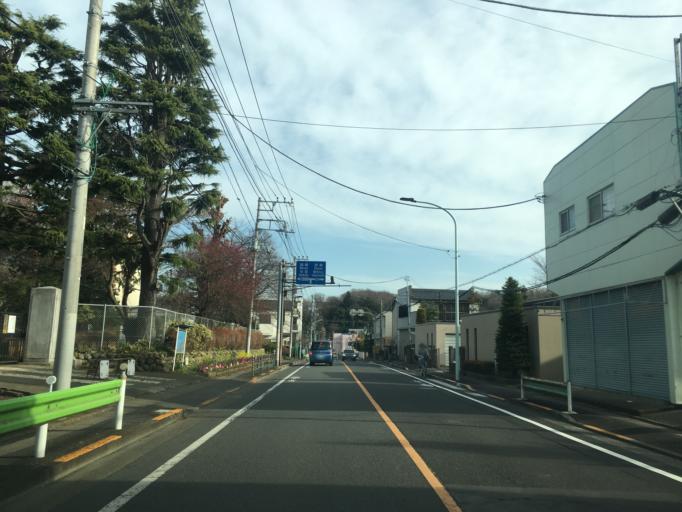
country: JP
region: Tokyo
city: Higashimurayama-shi
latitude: 35.7509
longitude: 139.4266
